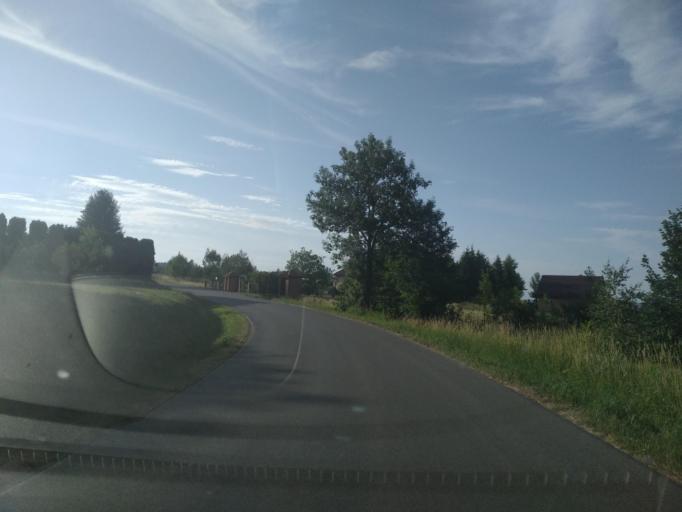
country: PL
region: Subcarpathian Voivodeship
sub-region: Powiat brzozowski
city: Gorki
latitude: 49.6545
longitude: 22.0332
